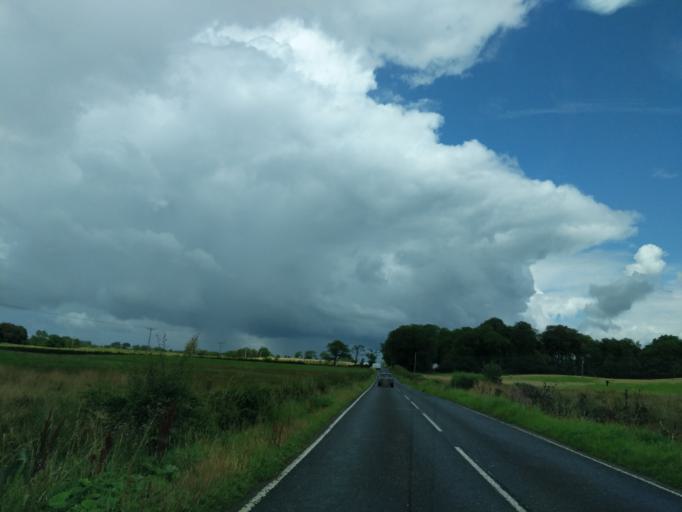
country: GB
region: Scotland
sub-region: East Ayrshire
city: Stewarton
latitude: 55.7114
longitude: -4.5176
